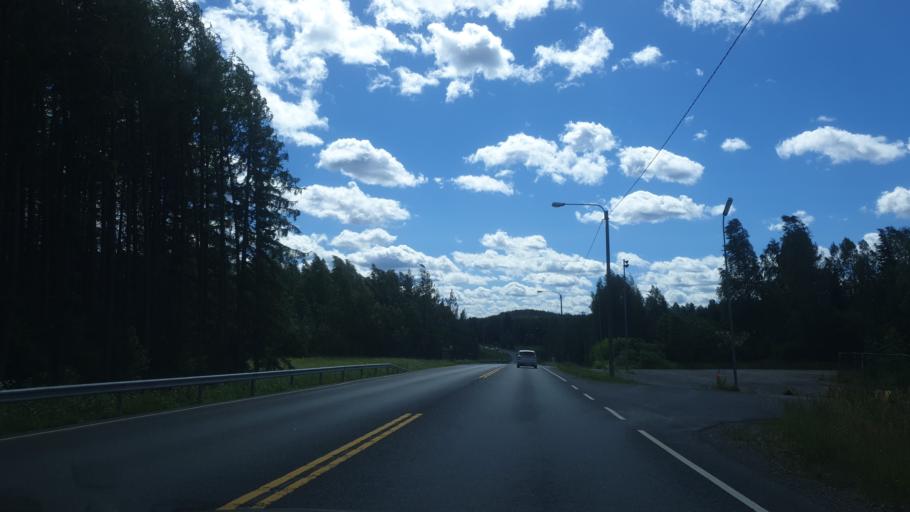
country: FI
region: Northern Savo
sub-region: Varkaus
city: Leppaevirta
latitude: 62.6416
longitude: 27.6087
